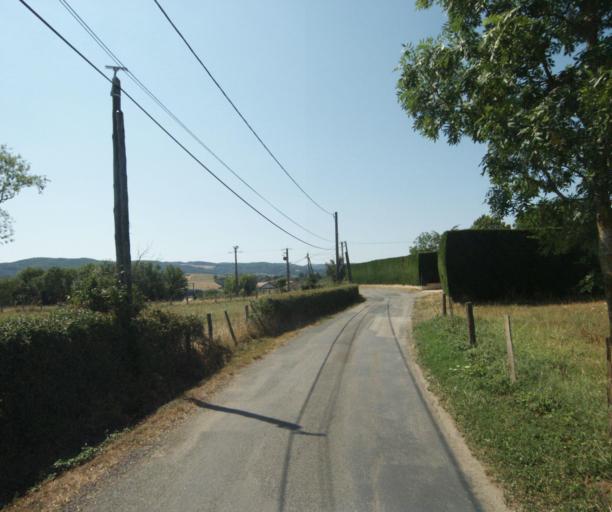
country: FR
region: Rhone-Alpes
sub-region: Departement du Rhone
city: Sourcieux-les-Mines
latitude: 45.8073
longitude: 4.6170
